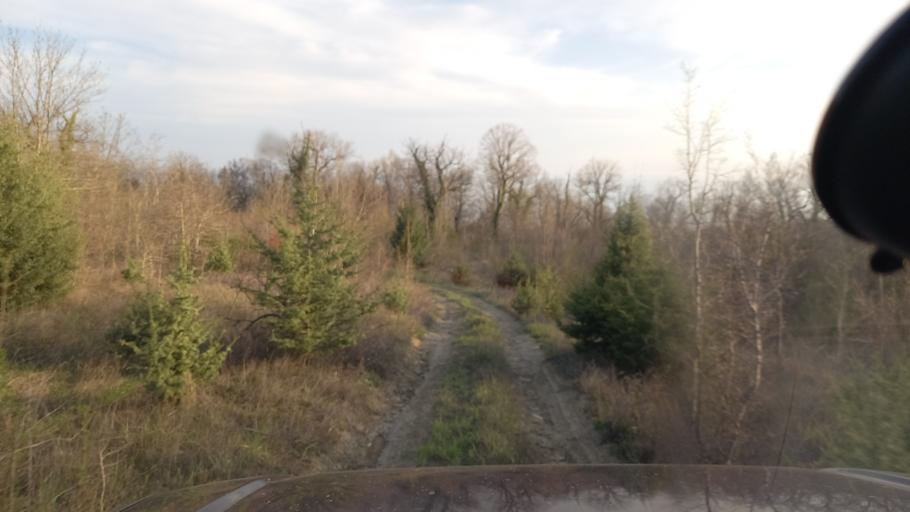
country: RU
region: Krasnodarskiy
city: Arkhipo-Osipovka
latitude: 44.3598
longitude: 38.5677
